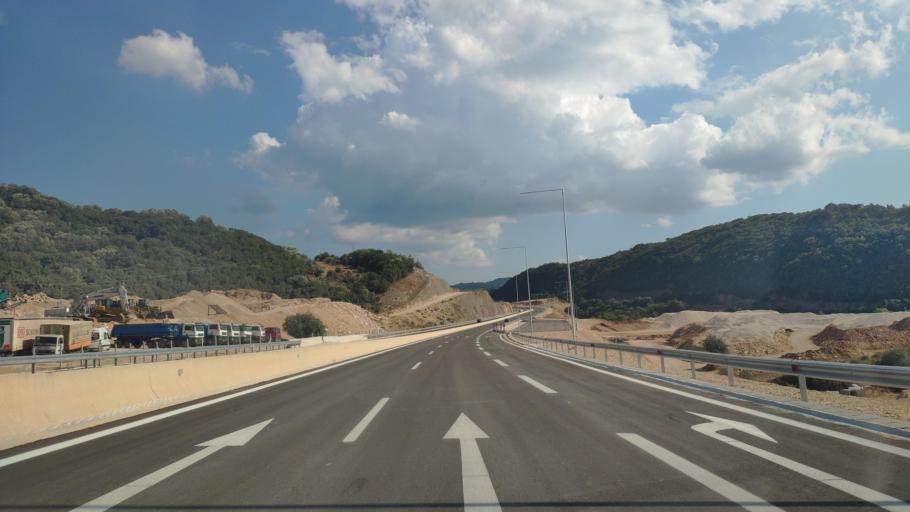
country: GR
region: West Greece
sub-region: Nomos Aitolias kai Akarnanias
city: Katouna
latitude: 38.7910
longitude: 21.1416
